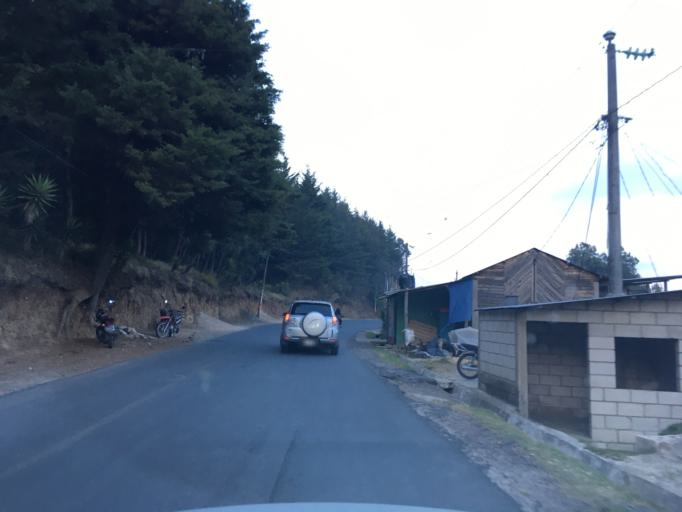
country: GT
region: Chimaltenango
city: Tecpan Guatemala
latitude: 14.7458
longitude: -91.0030
